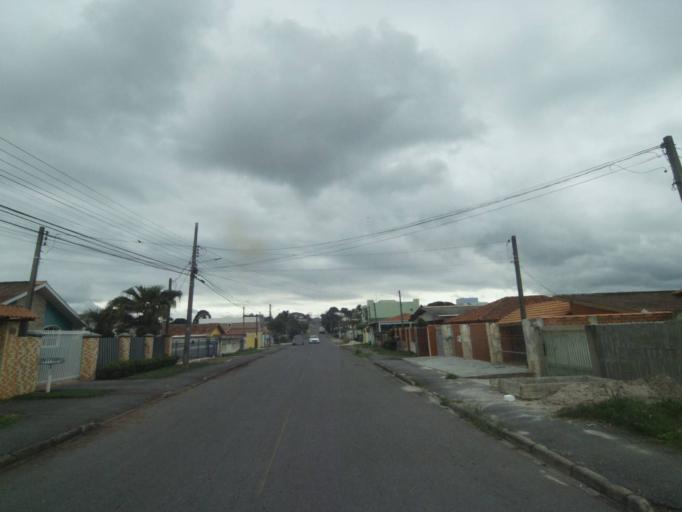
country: BR
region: Parana
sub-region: Quatro Barras
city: Quatro Barras
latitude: -25.3510
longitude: -49.1085
